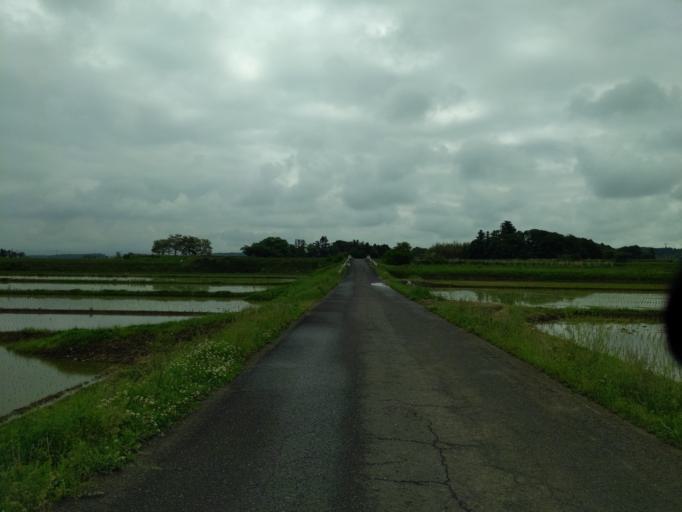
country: JP
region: Fukushima
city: Koriyama
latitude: 37.3503
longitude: 140.2792
